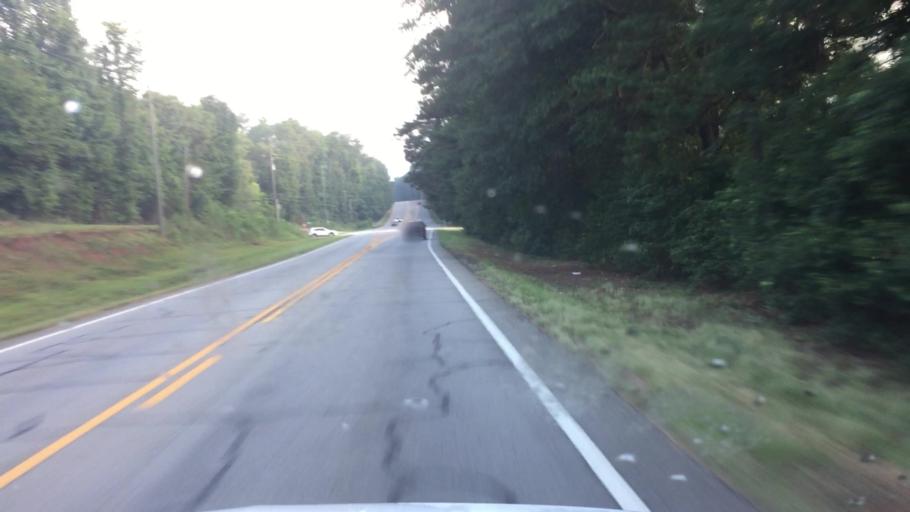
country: US
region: Georgia
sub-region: DeKalb County
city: Pine Mountain
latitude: 33.6374
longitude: -84.1844
